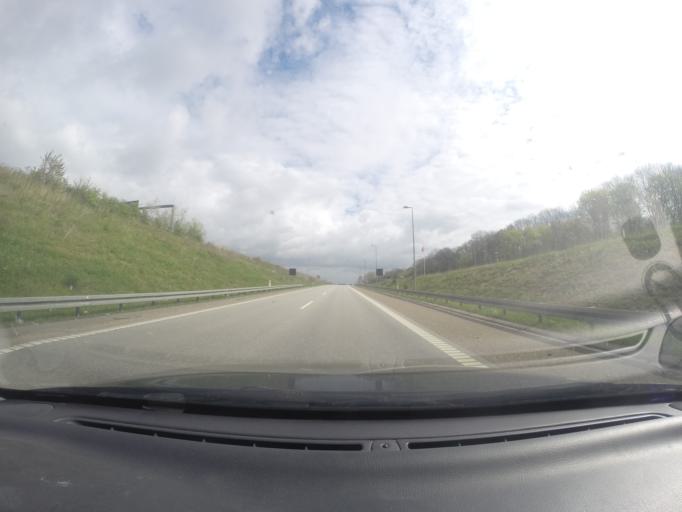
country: DK
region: Capital Region
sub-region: Rodovre Kommune
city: Rodovre
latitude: 55.6923
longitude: 12.4369
